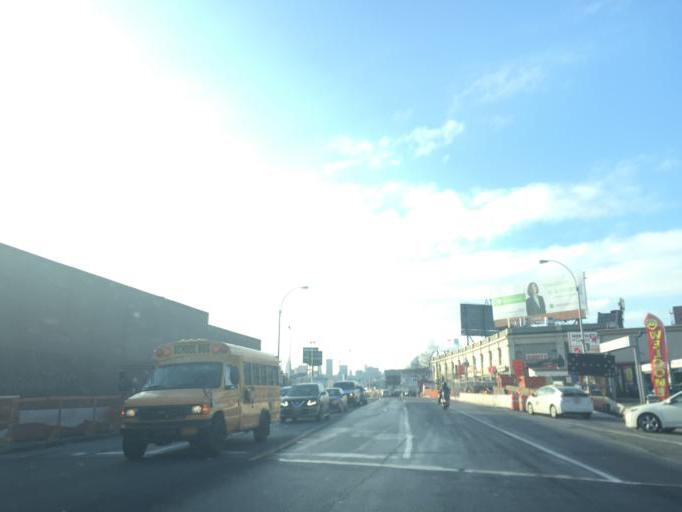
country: US
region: New York
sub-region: Queens County
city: Long Island City
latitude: 40.7539
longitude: -73.9154
